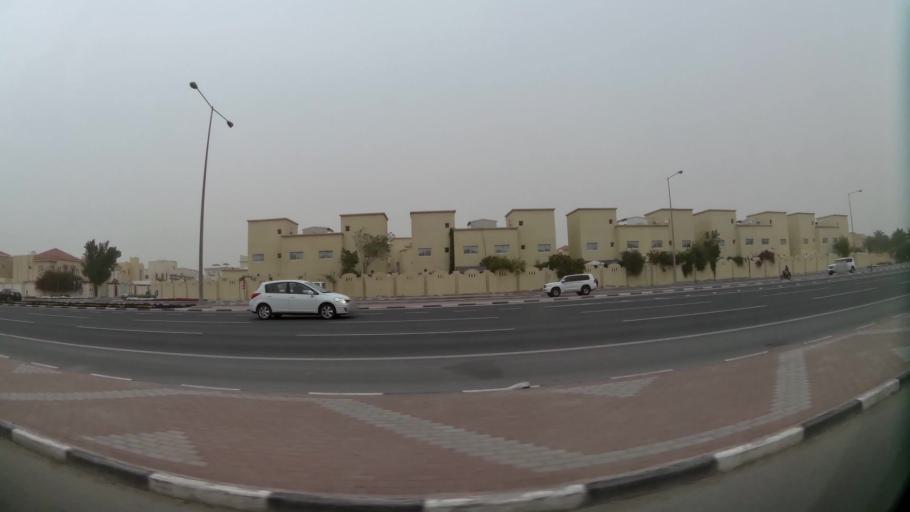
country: QA
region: Baladiyat ad Dawhah
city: Doha
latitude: 25.2463
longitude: 51.4918
